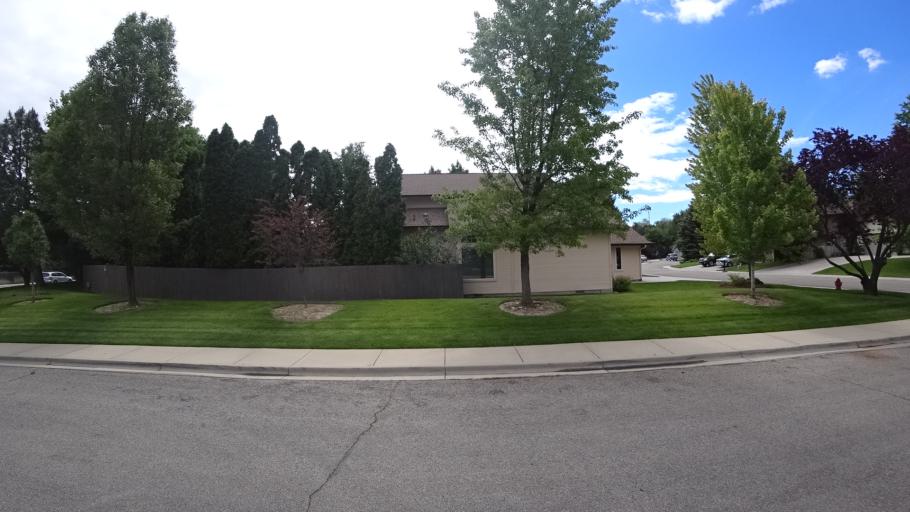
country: US
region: Idaho
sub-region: Ada County
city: Boise
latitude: 43.5675
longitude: -116.1756
